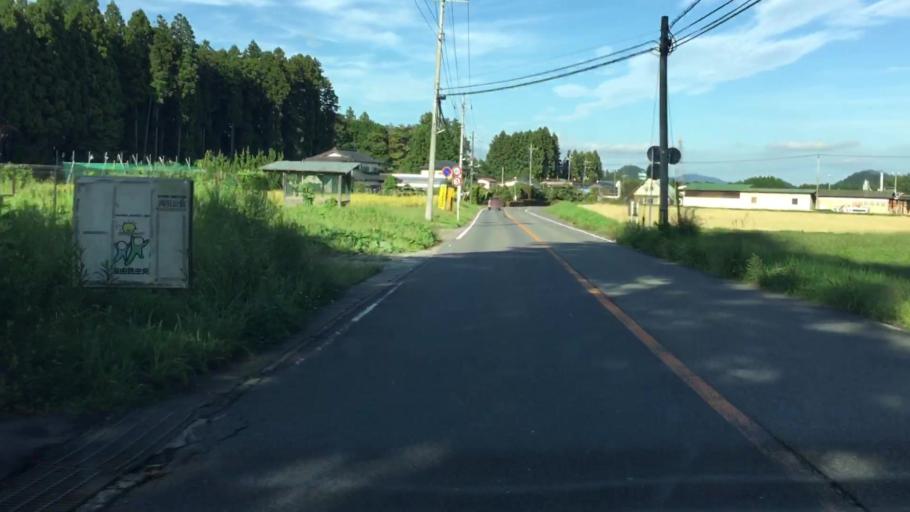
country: JP
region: Tochigi
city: Imaichi
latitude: 36.7361
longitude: 139.7024
